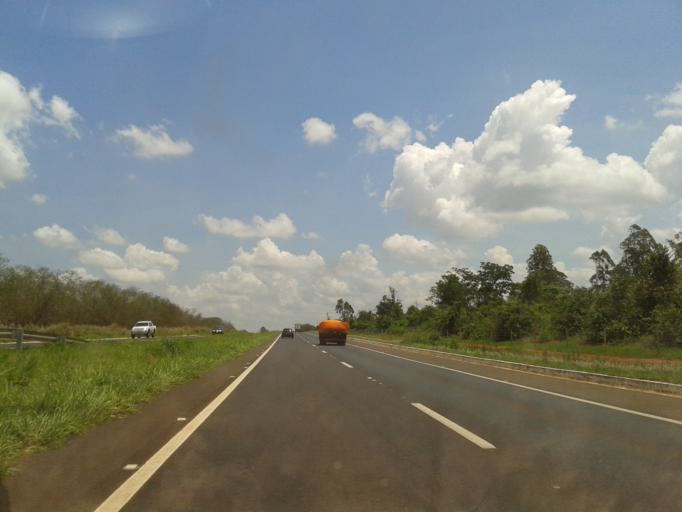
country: BR
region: Minas Gerais
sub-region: Uberlandia
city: Uberlandia
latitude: -18.8770
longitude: -48.5160
